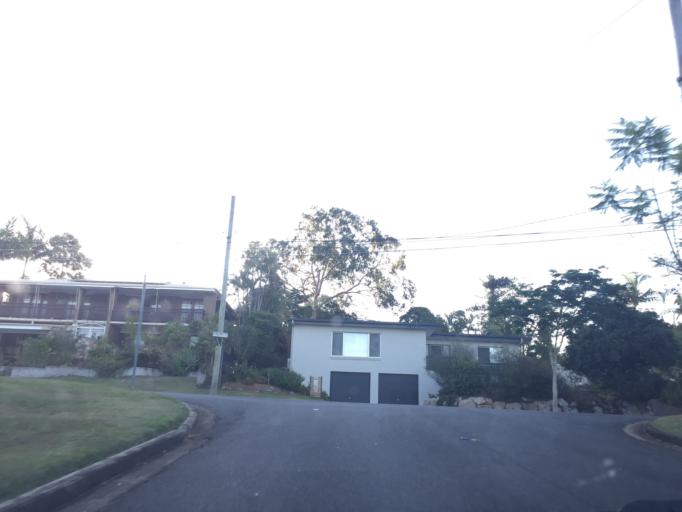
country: AU
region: Queensland
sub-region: Brisbane
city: Taringa
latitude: -27.4535
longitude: 152.9471
